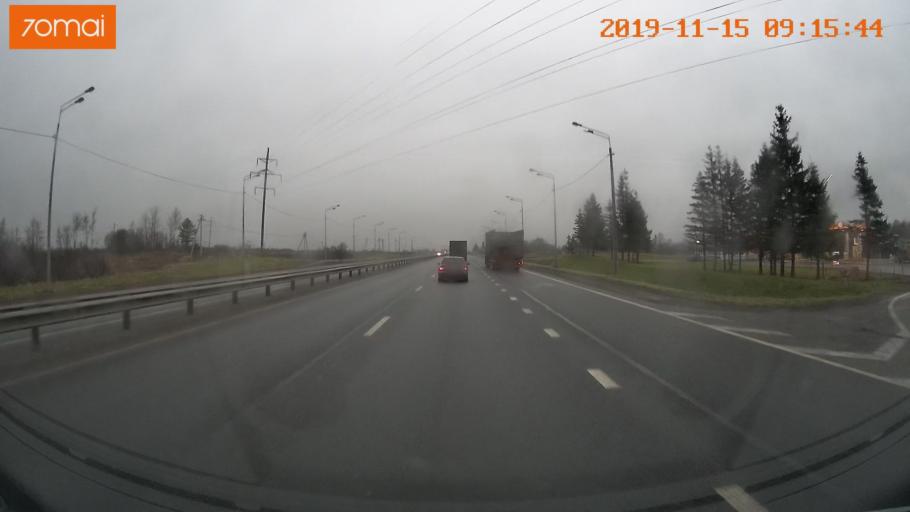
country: RU
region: Vologda
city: Tonshalovo
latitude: 59.2409
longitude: 37.9679
